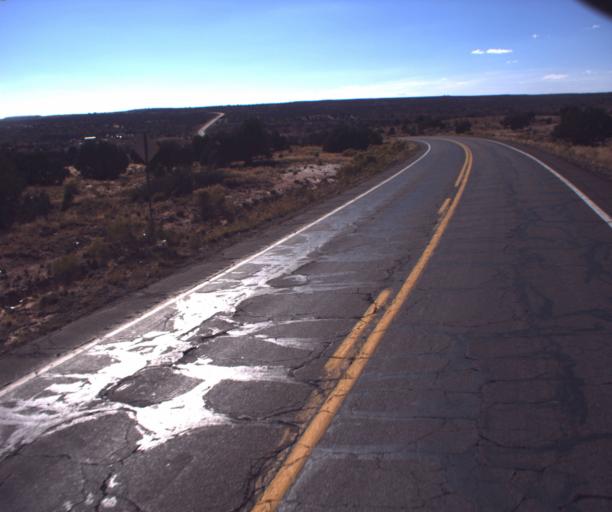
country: US
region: Arizona
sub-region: Coconino County
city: Kaibito
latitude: 36.6134
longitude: -111.0691
